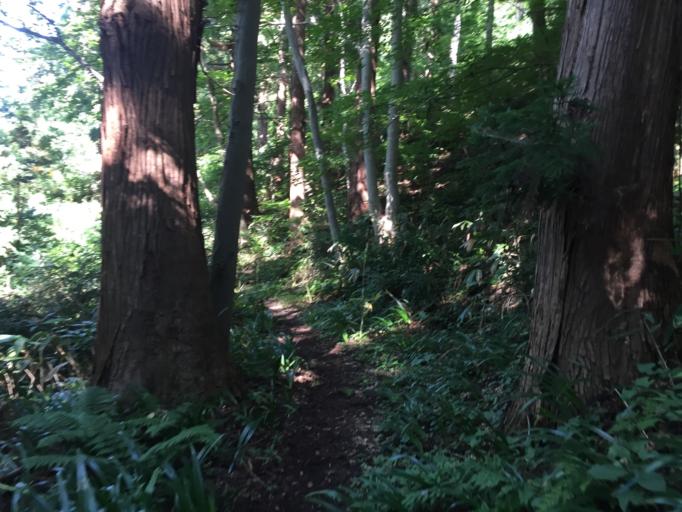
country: JP
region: Fukushima
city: Inawashiro
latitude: 37.4855
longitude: 139.9563
